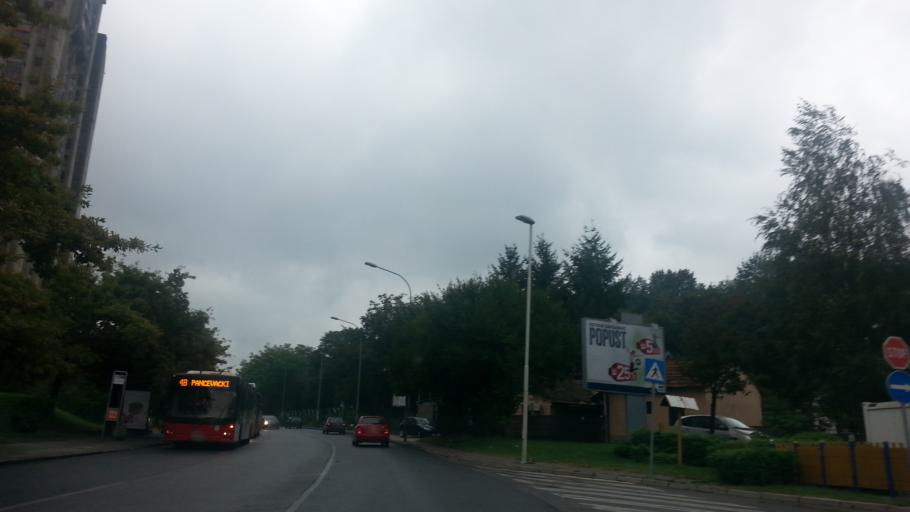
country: RS
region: Central Serbia
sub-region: Belgrade
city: Vozdovac
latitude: 44.7605
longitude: 20.4732
